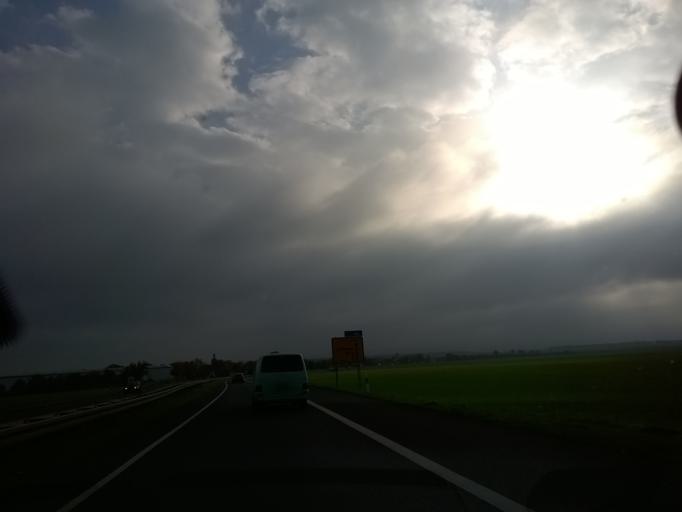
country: DE
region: Thuringia
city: Andisleben
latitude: 51.0877
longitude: 10.9277
